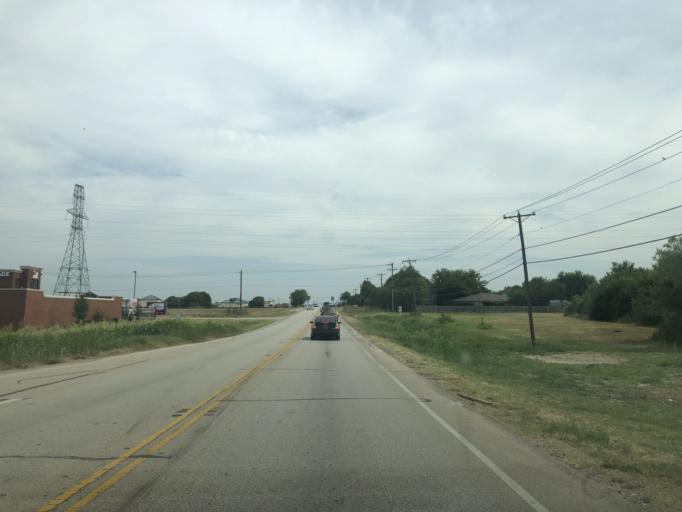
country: US
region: Texas
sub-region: Tarrant County
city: Blue Mound
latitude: 32.8765
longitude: -97.3425
